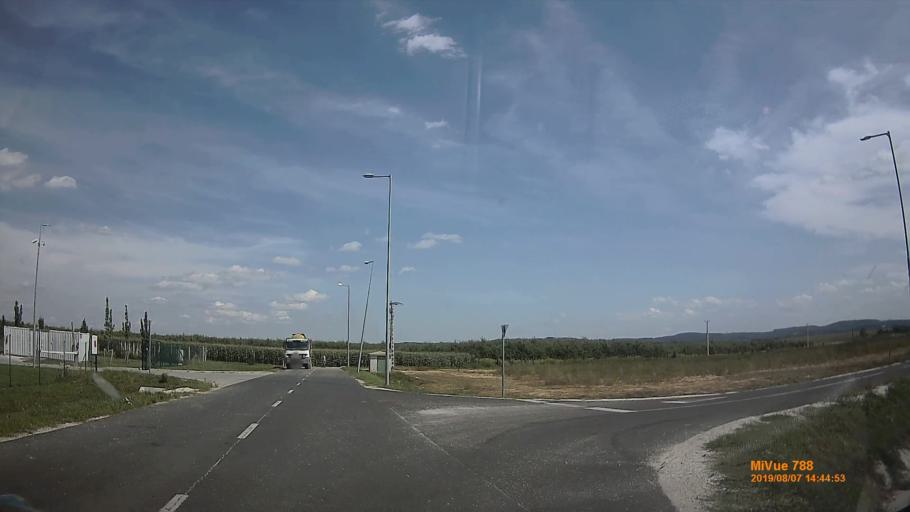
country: HU
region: Zala
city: Zalaegerszeg
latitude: 46.8769
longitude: 16.8415
